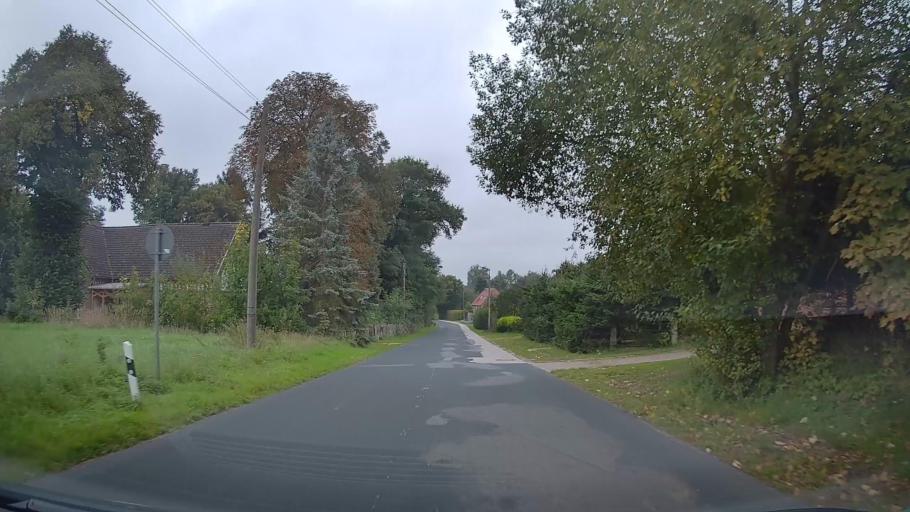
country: DE
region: Mecklenburg-Vorpommern
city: Kavelstorf
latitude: 53.9246
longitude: 12.2005
